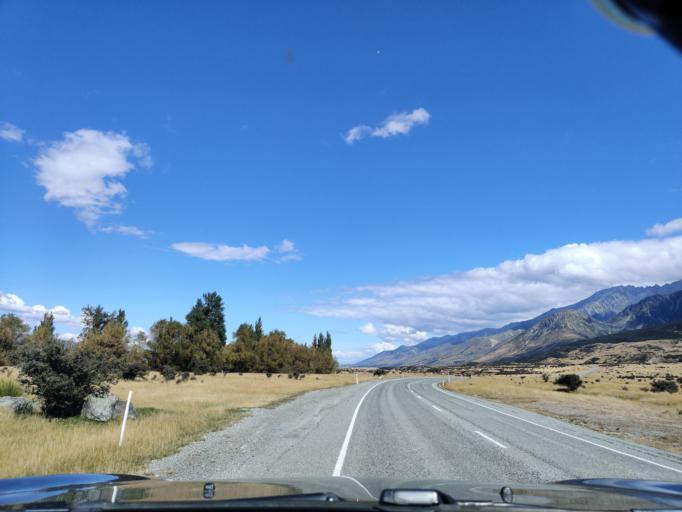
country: NZ
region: Canterbury
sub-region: Timaru District
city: Pleasant Point
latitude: -43.7890
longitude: 170.1196
